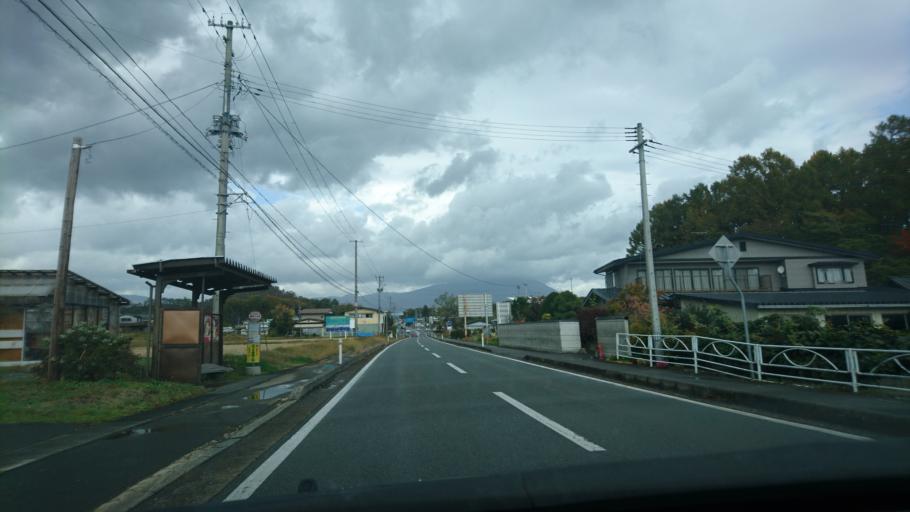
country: JP
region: Iwate
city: Shizukuishi
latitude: 39.6950
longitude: 141.0237
